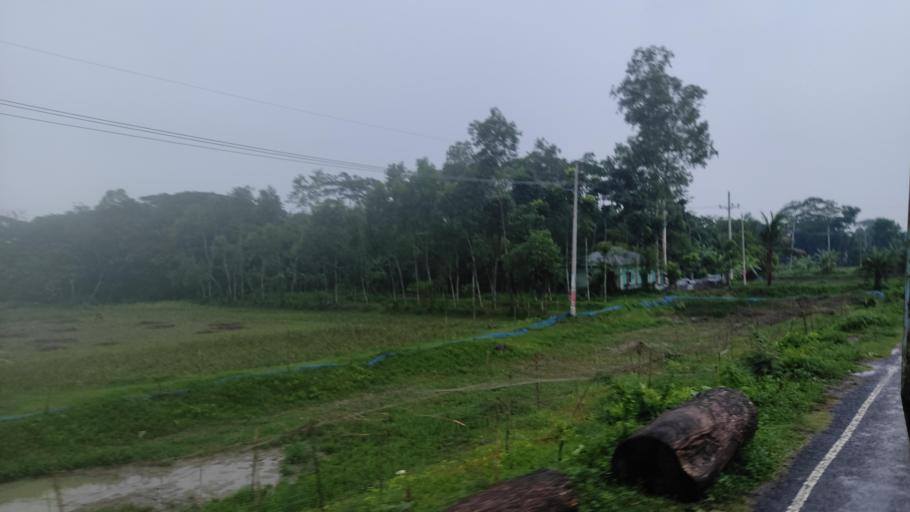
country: BD
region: Barisal
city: Bhandaria
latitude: 22.2922
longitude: 90.3254
